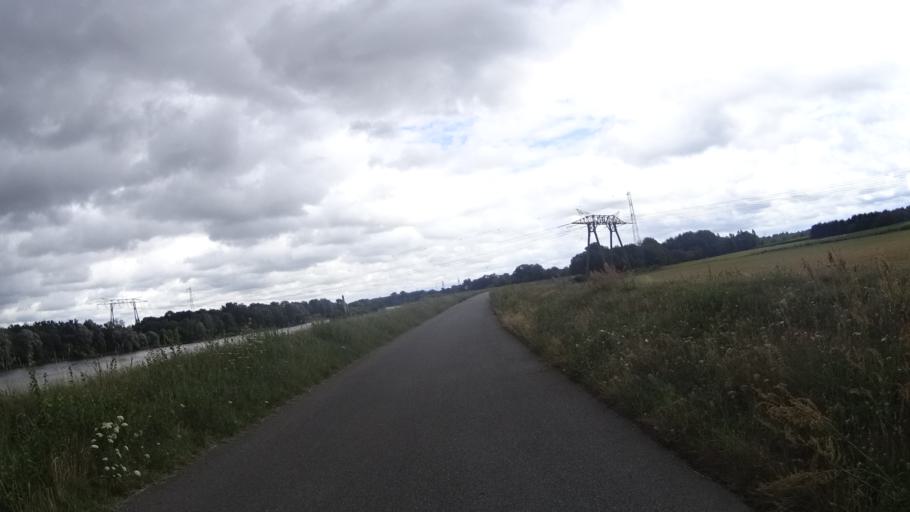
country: FR
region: Centre
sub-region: Departement du Loiret
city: Mareau-aux-Pres
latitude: 47.8636
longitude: 1.7922
